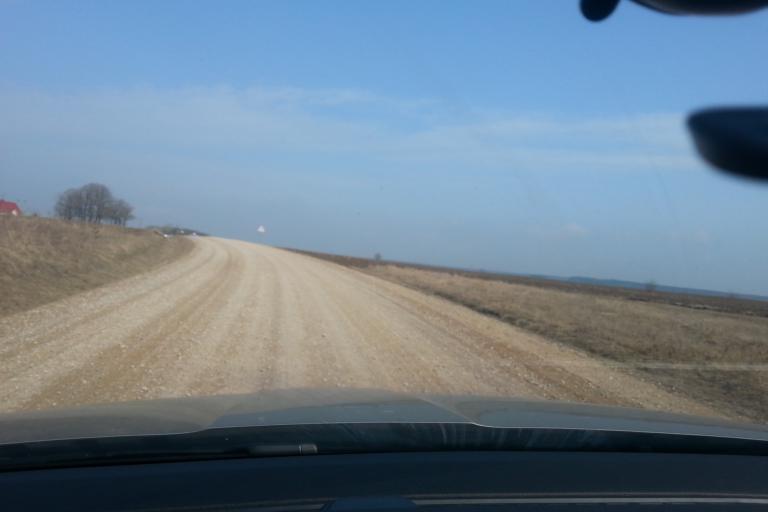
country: LT
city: Trakai
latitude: 54.5834
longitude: 24.9762
